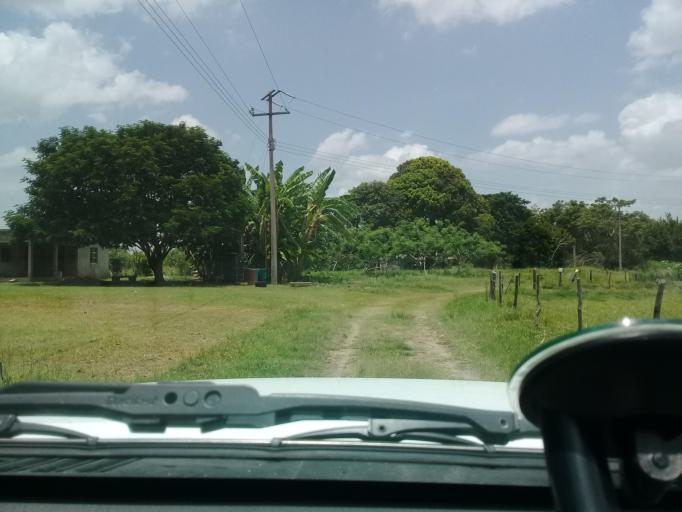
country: MX
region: Veracruz
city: Moralillo
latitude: 22.1320
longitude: -98.0345
